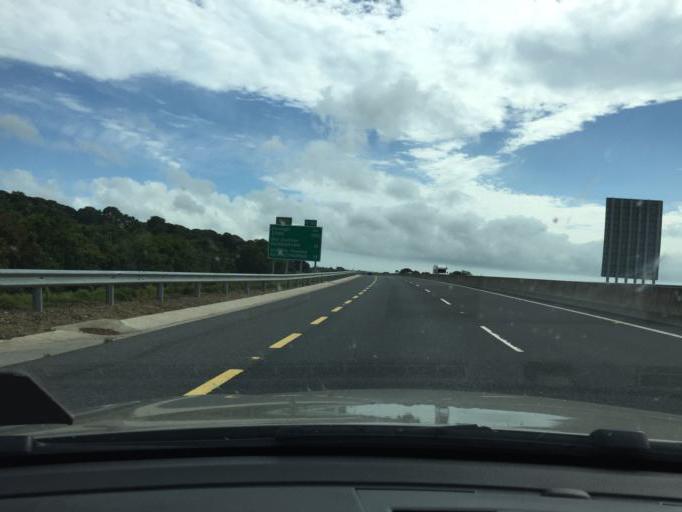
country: IE
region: Leinster
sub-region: Kilkenny
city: Mooncoin
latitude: 52.2525
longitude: -7.1904
